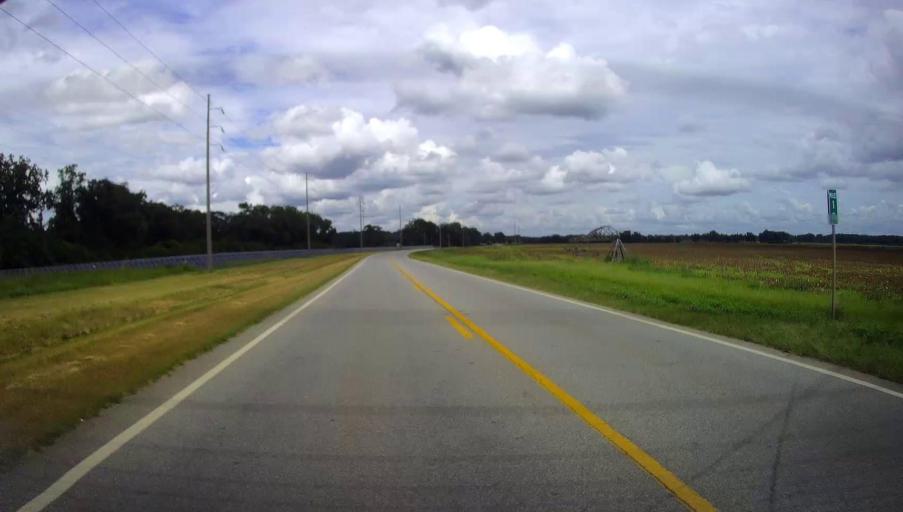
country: US
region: Georgia
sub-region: Macon County
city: Oglethorpe
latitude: 32.2786
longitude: -84.0650
